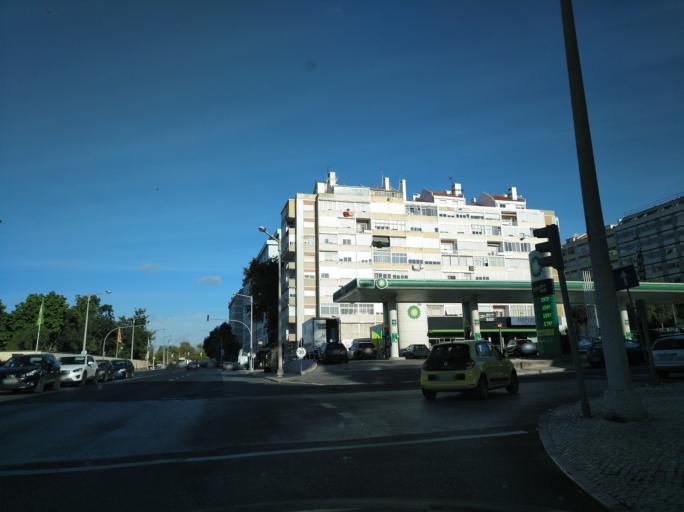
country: PT
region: Lisbon
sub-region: Odivelas
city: Pontinha
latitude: 38.7586
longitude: -9.1802
